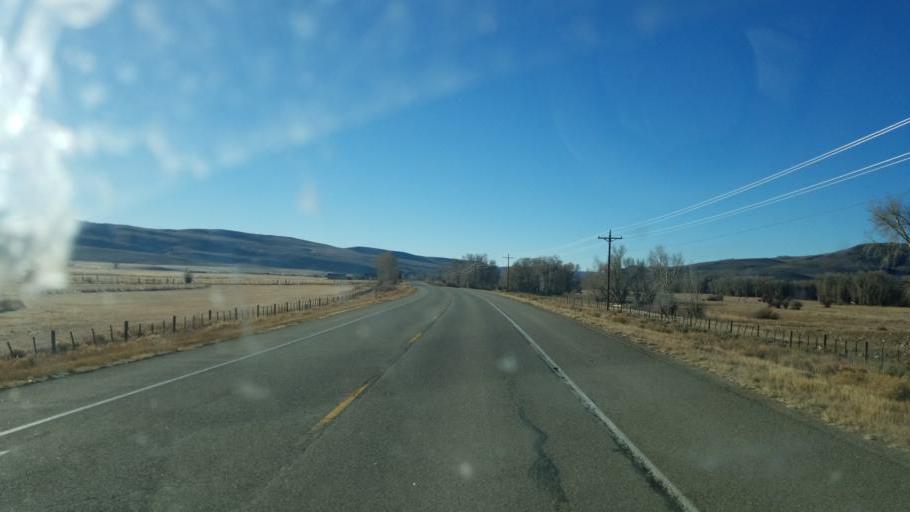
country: US
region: Colorado
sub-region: Gunnison County
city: Crested Butte
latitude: 38.7520
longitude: -106.8602
